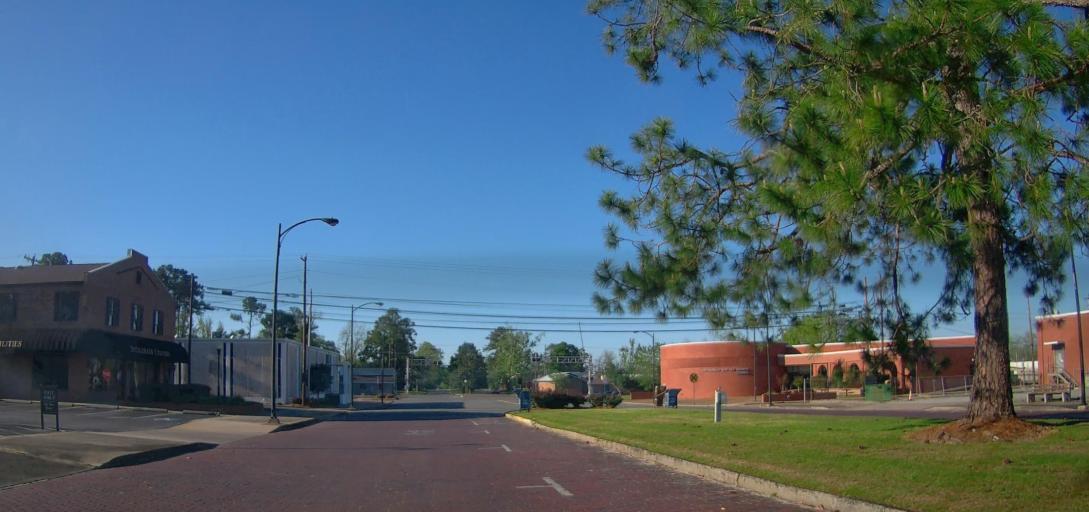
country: US
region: Georgia
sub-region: Ben Hill County
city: Fitzgerald
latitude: 31.7153
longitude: -83.2542
